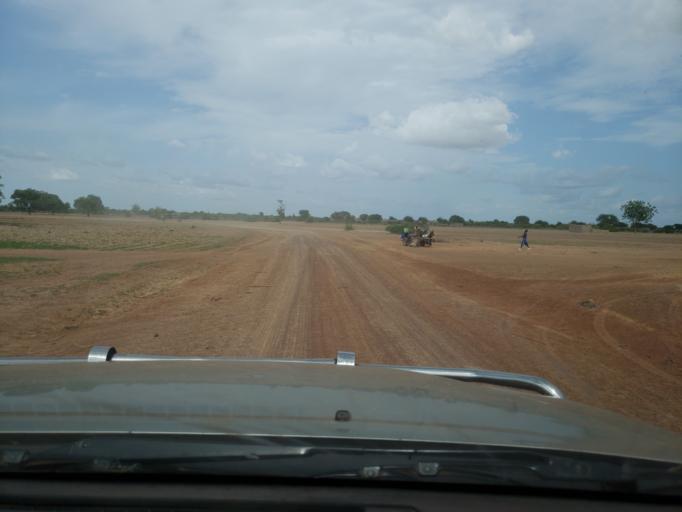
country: ML
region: Segou
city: Bla
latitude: 12.7433
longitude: -5.6391
